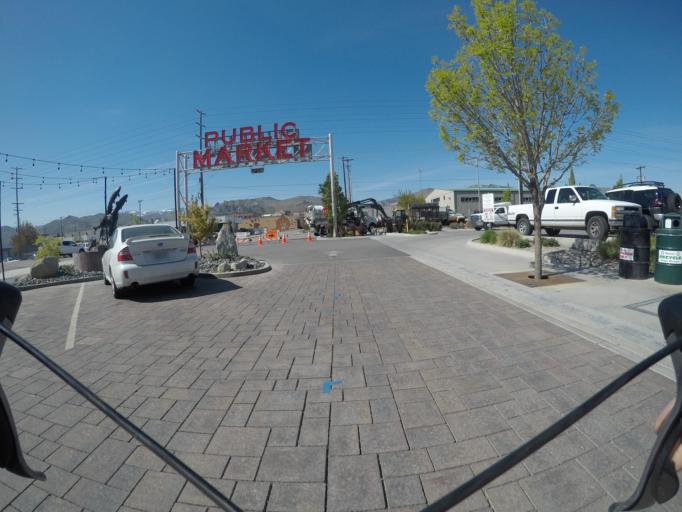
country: US
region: Washington
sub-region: Chelan County
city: Wenatchee
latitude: 47.4247
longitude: -120.3071
